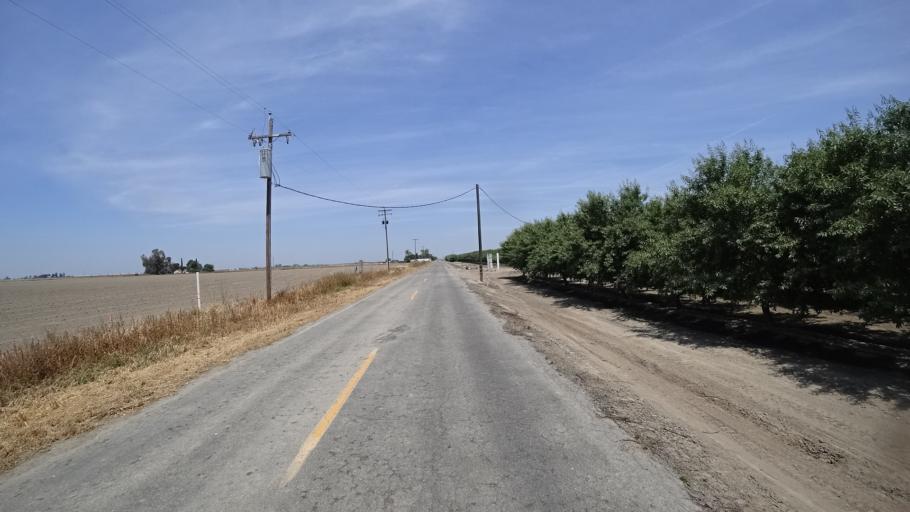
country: US
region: California
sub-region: Fresno County
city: Riverdale
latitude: 36.3905
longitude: -119.8962
